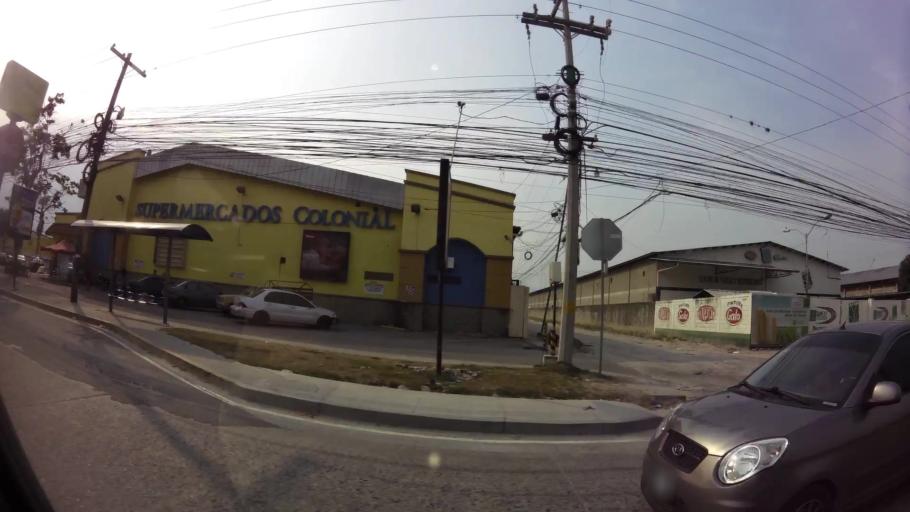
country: HN
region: Cortes
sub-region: San Pedro Sula
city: Pena Blanca
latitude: 15.5503
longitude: -88.0046
